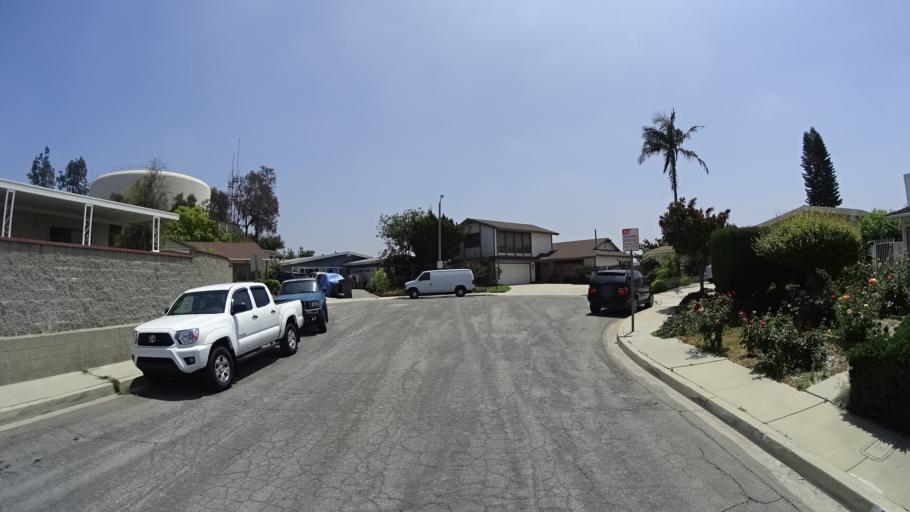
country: US
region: California
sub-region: Los Angeles County
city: Monterey Park
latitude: 34.0588
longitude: -118.1490
